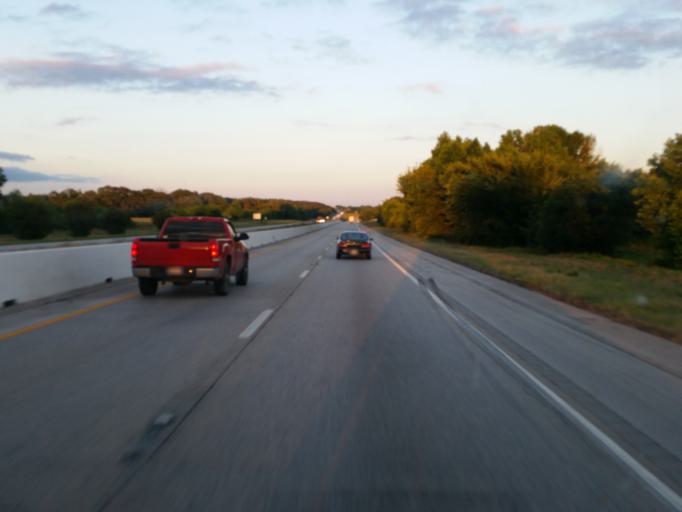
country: US
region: Texas
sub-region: Smith County
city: Hideaway
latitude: 32.4903
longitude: -95.5504
